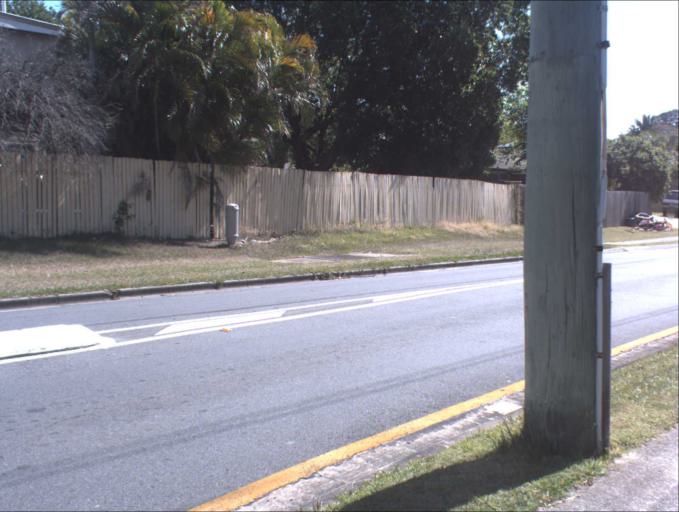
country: AU
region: Queensland
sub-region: Logan
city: Logan City
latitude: -27.6460
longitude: 153.1279
